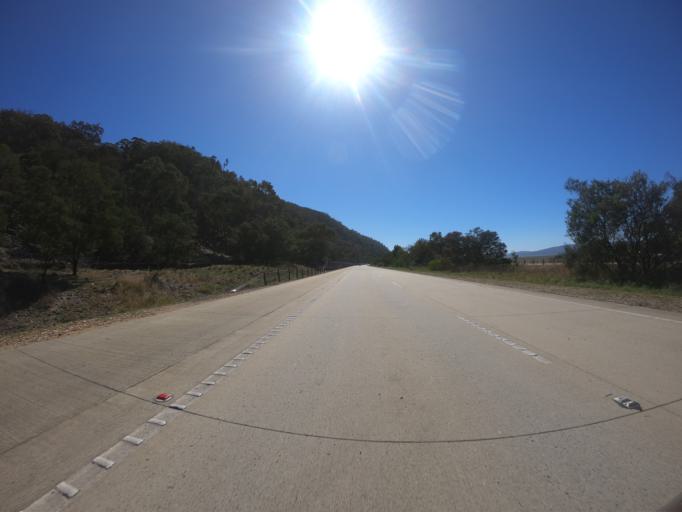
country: AU
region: New South Wales
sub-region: Yass Valley
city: Gundaroo
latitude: -35.0667
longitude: 149.3734
